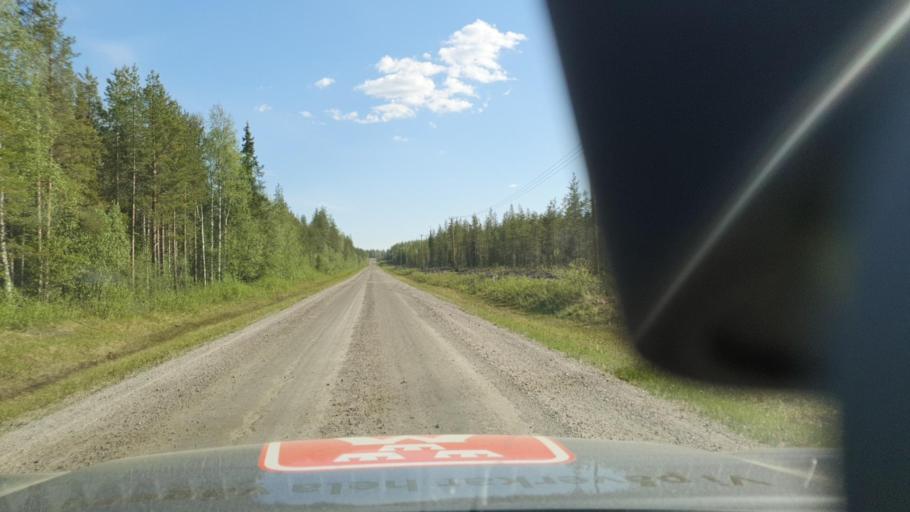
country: SE
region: Norrbotten
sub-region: Bodens Kommun
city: Boden
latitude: 66.5014
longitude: 21.9076
